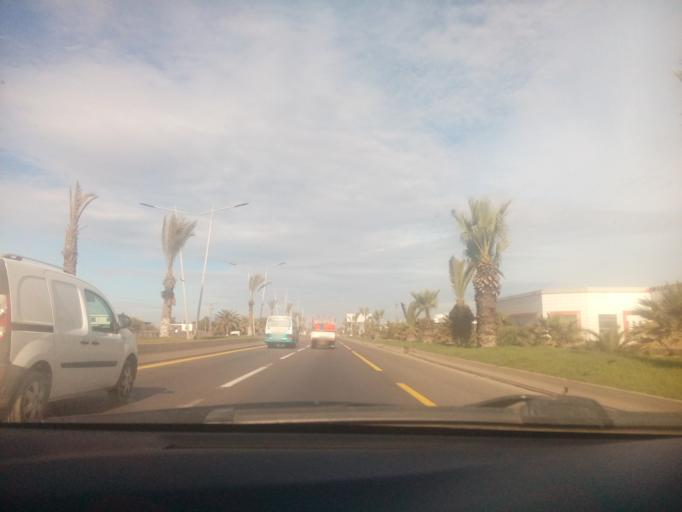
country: DZ
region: Oran
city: Es Senia
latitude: 35.6491
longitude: -0.5906
